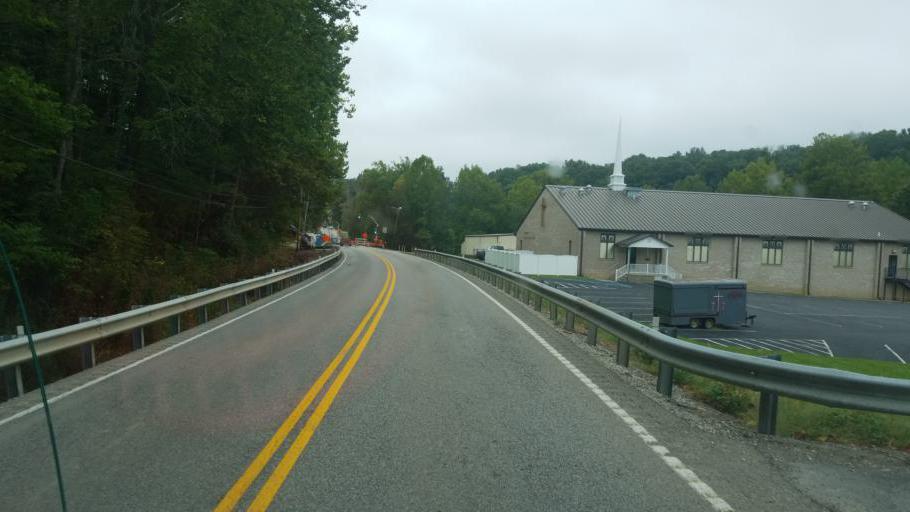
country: US
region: Kentucky
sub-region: Rowan County
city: Morehead
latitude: 38.2100
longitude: -83.4695
